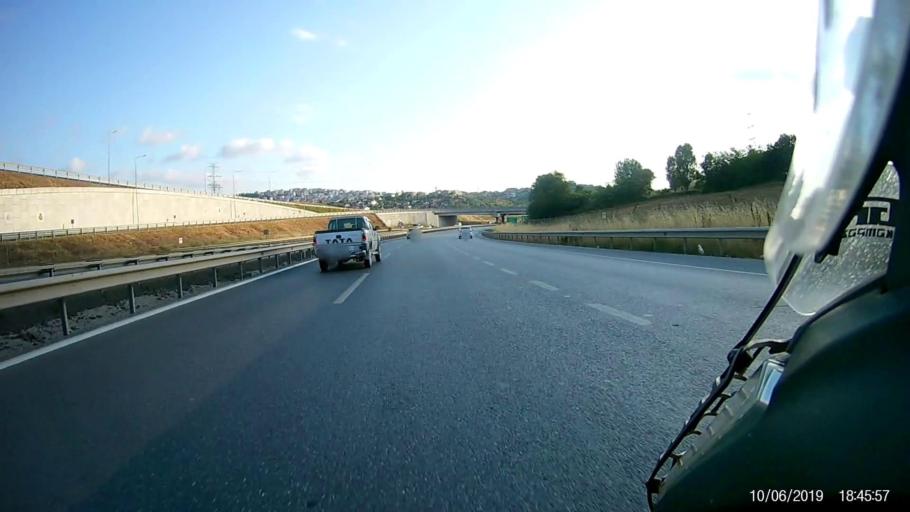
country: TR
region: Istanbul
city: Sancaktepe
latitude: 41.0300
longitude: 29.2654
